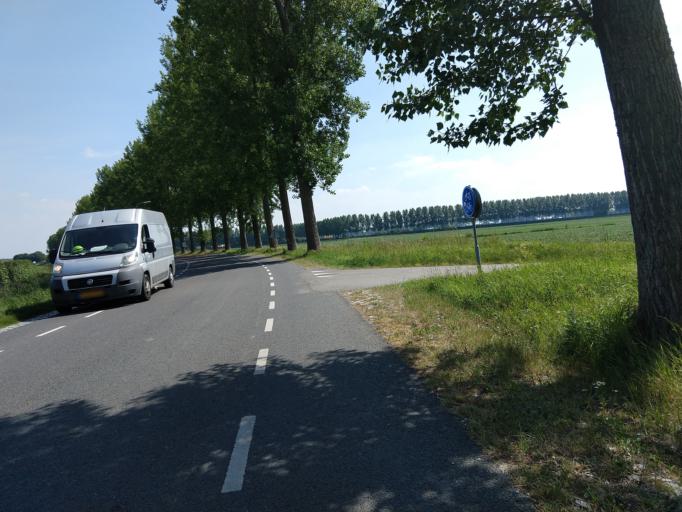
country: NL
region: Zeeland
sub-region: Gemeente Borsele
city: Borssele
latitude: 51.4403
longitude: 3.7995
